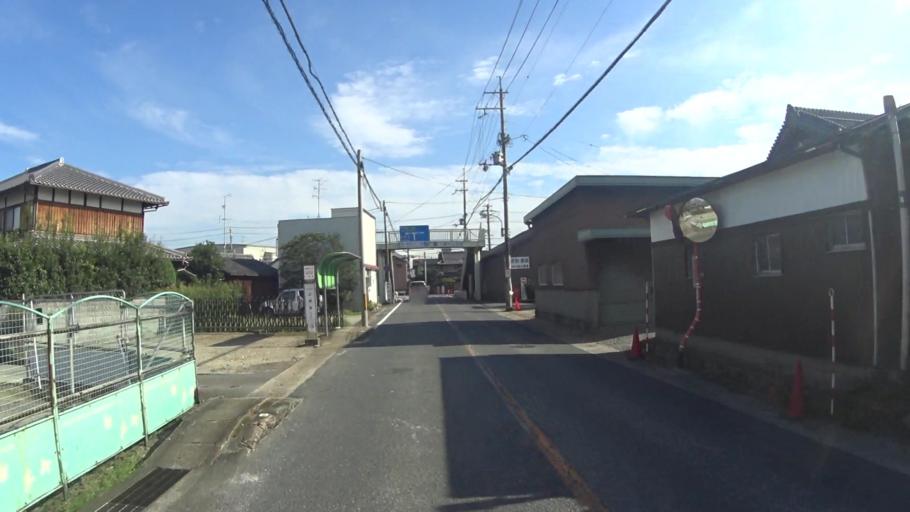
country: JP
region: Kyoto
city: Yawata
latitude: 34.8692
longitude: 135.7310
